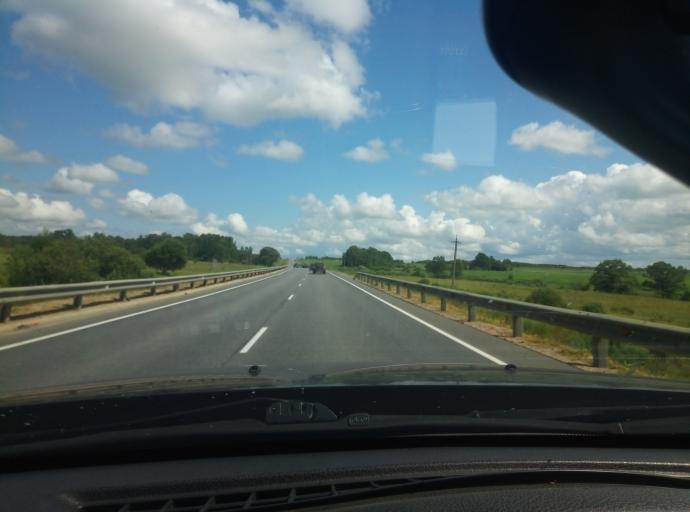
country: RU
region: Tula
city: Dubna
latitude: 54.3006
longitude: 37.0551
